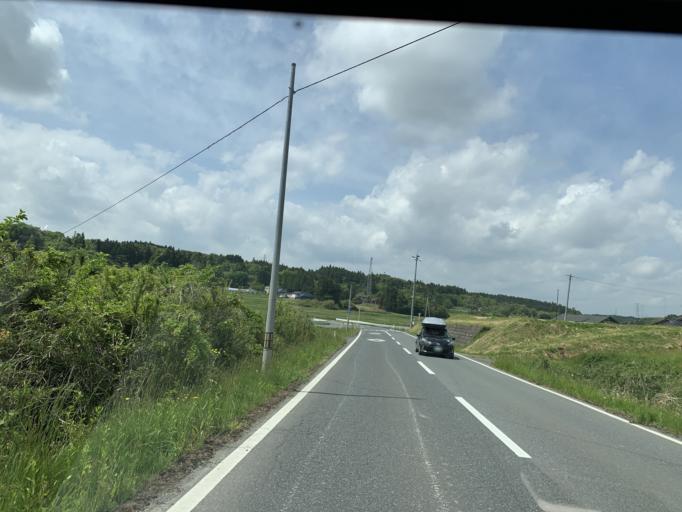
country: JP
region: Iwate
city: Ichinoseki
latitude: 38.7821
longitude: 140.9995
